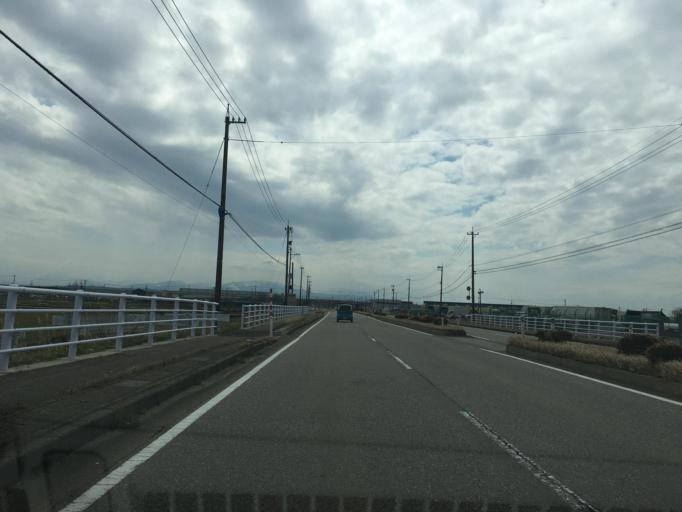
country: JP
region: Toyama
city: Kuragaki-kosugi
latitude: 36.7340
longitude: 137.1270
